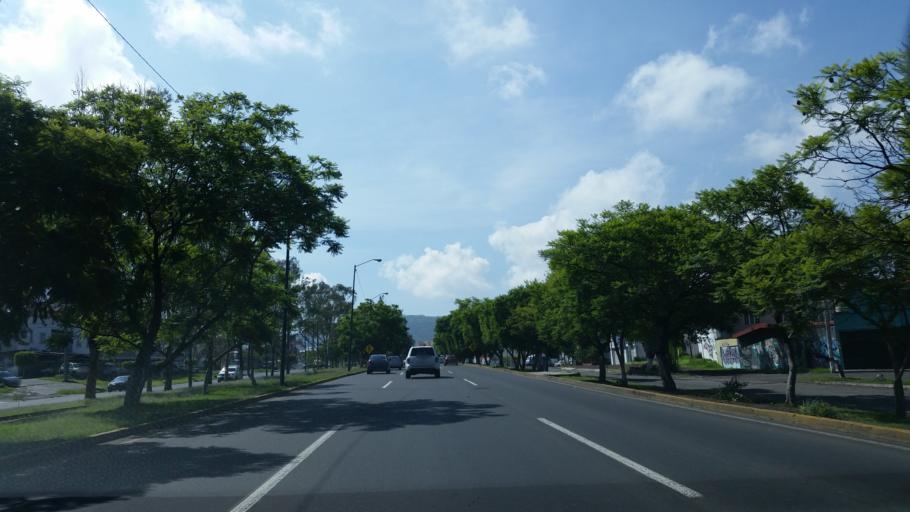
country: MX
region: Michoacan
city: Morelia
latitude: 19.7021
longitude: -101.1572
